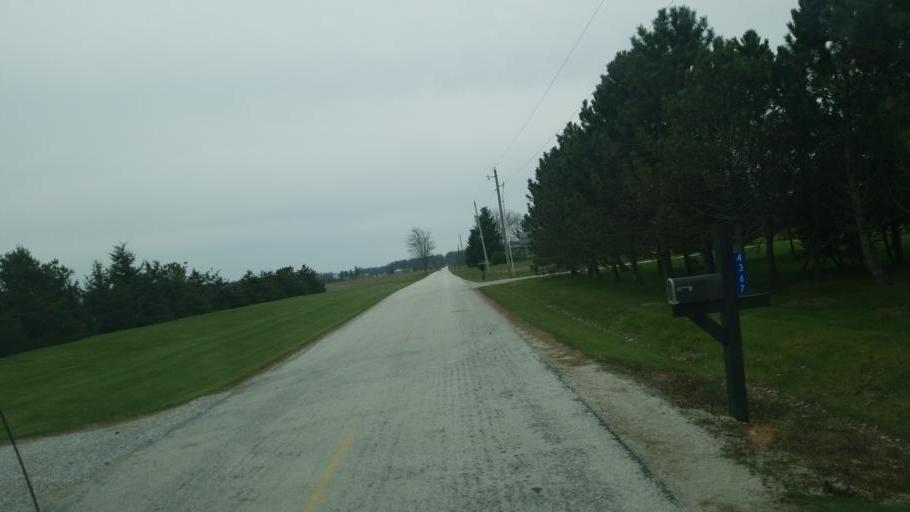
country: US
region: Ohio
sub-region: Seneca County
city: Fostoria
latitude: 41.0593
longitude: -83.4208
